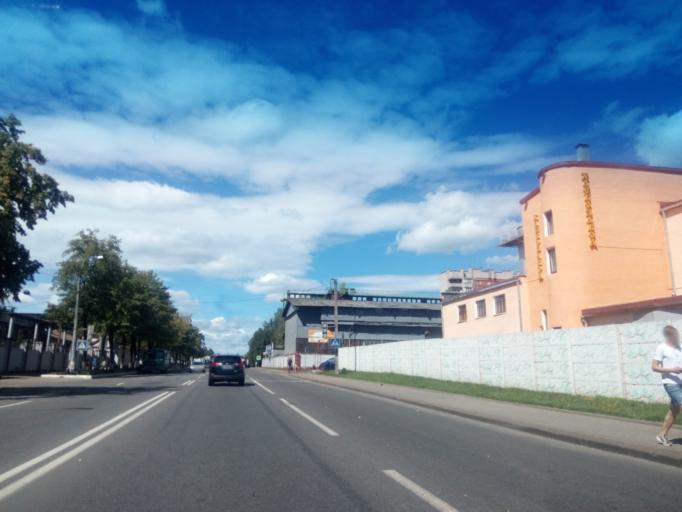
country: BY
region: Vitebsk
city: Polatsk
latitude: 55.4919
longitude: 28.7772
